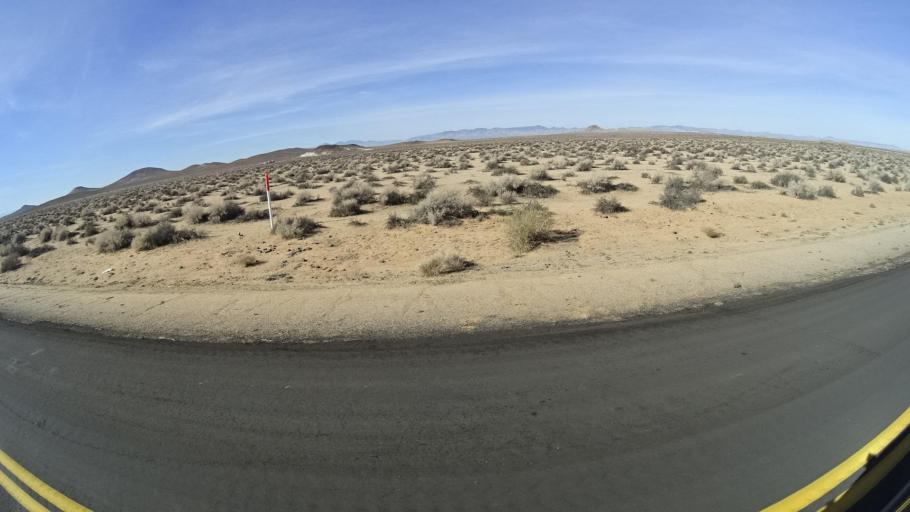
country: US
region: California
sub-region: Kern County
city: North Edwards
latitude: 35.0754
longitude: -117.7928
